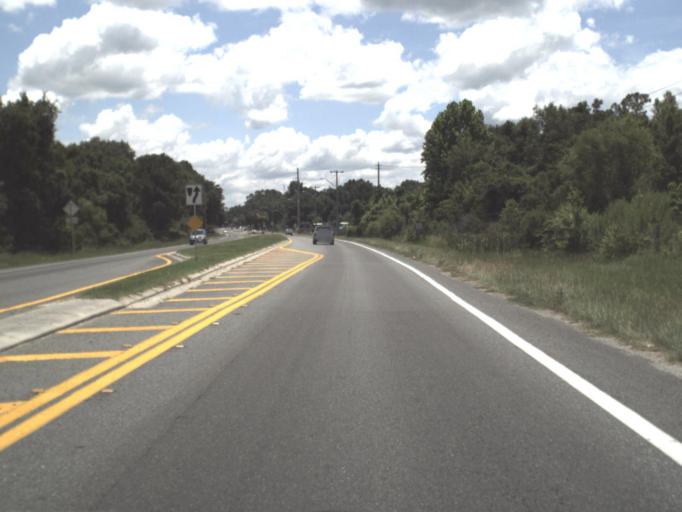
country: US
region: Florida
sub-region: Columbia County
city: Five Points
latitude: 30.2062
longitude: -82.6467
